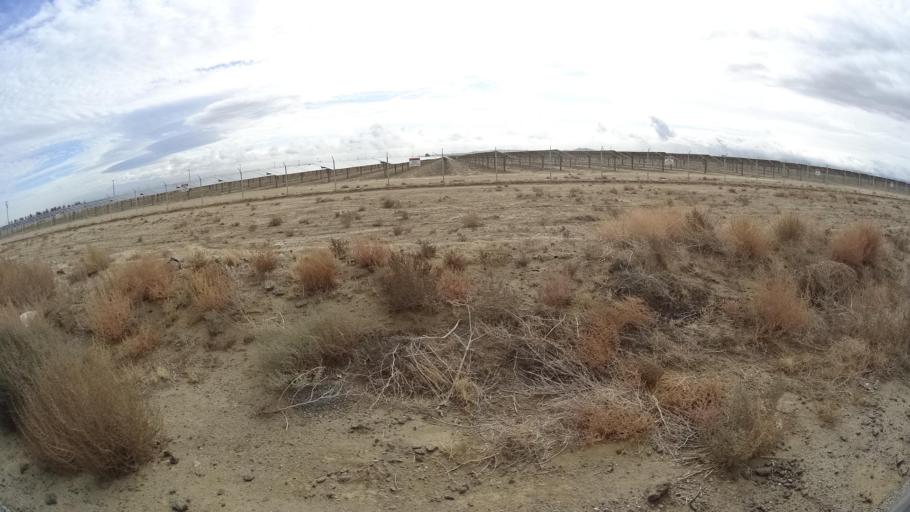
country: US
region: California
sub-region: Kern County
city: Rosamond
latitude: 34.8630
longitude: -118.3637
